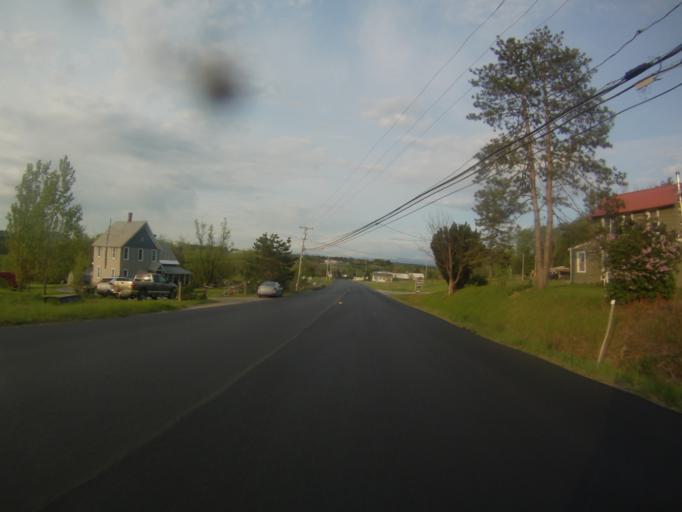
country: US
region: New York
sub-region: Essex County
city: Ticonderoga
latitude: 43.8431
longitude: -73.4501
